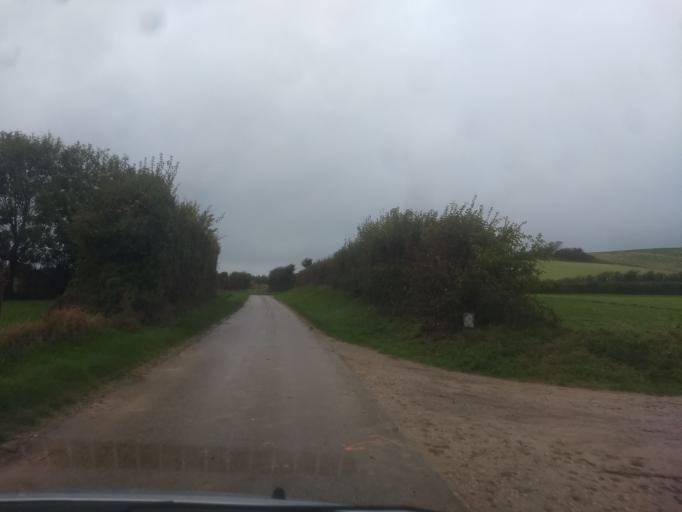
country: FR
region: Nord-Pas-de-Calais
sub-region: Departement du Pas-de-Calais
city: Wissant
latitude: 50.8931
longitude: 1.6901
